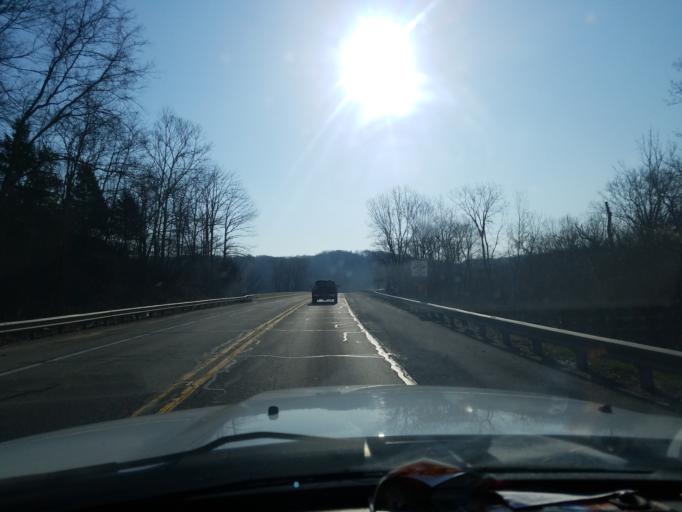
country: US
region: Indiana
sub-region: Owen County
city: Spencer
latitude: 39.2882
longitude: -86.7478
